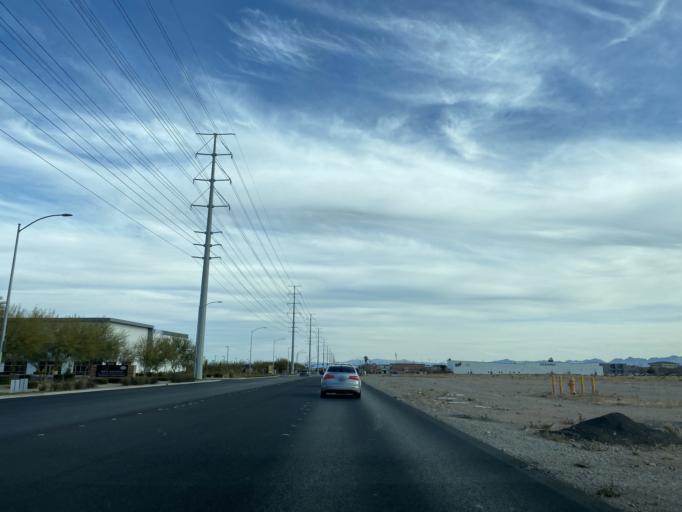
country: US
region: Nevada
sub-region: Clark County
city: Enterprise
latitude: 36.0556
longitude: -115.2656
